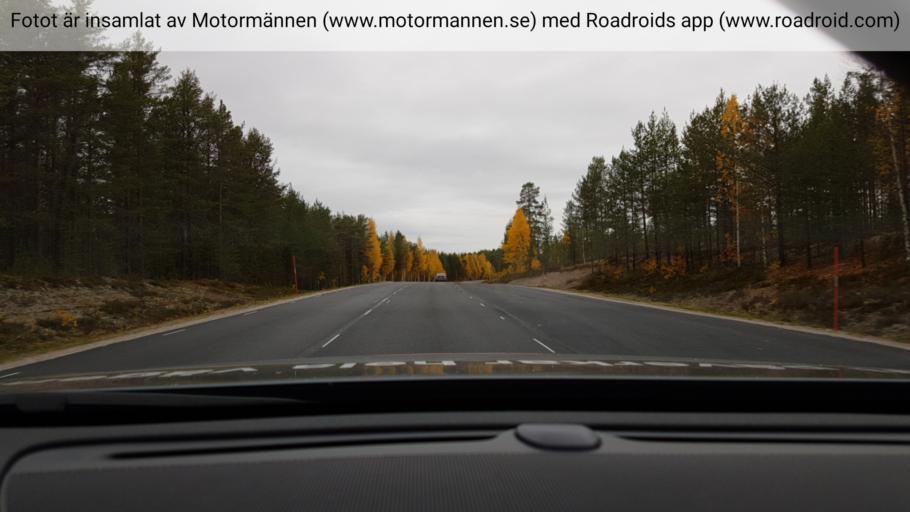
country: SE
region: Norrbotten
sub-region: Overkalix Kommun
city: OEverkalix
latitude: 66.4416
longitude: 22.7879
